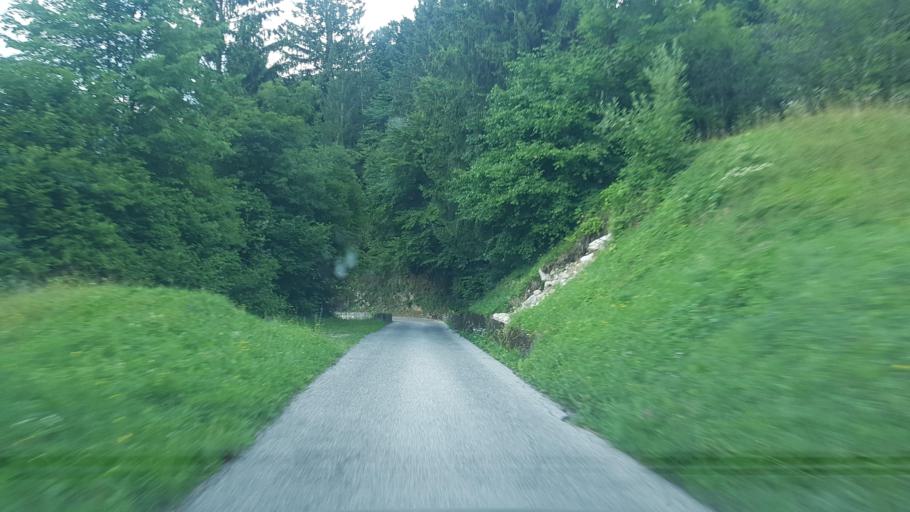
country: IT
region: Friuli Venezia Giulia
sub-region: Provincia di Udine
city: Paularo
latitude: 46.4825
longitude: 13.0992
